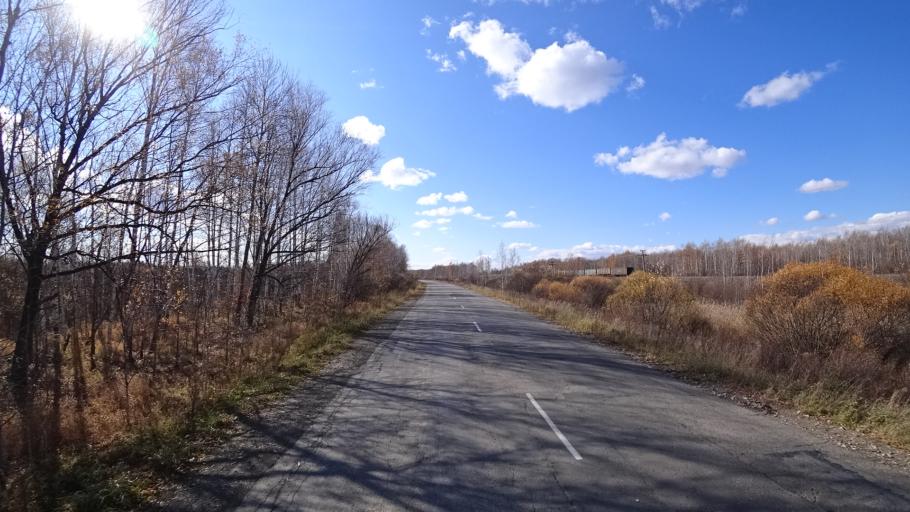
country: RU
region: Khabarovsk Krai
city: Amursk
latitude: 50.1139
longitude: 136.5238
